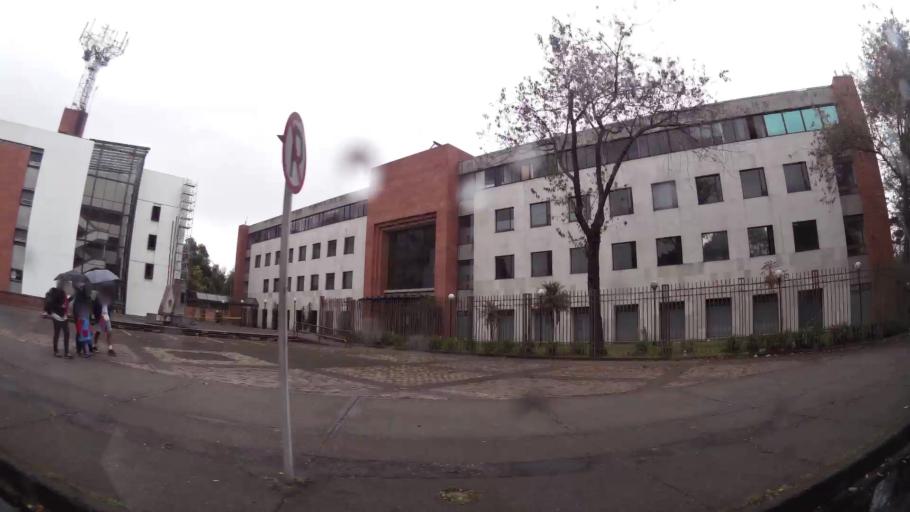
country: CO
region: Bogota D.C.
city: Bogota
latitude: 4.6597
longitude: -74.1046
